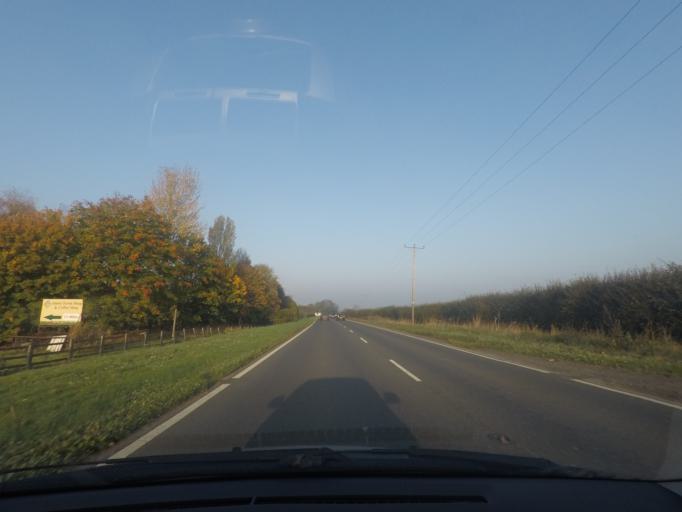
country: GB
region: England
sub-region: City of York
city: Askham Richard
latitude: 53.9912
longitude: -1.2356
